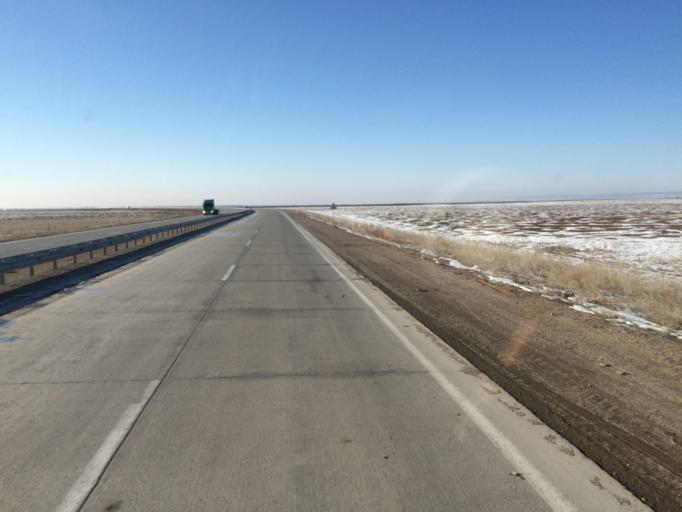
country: KG
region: Chuy
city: Sokuluk
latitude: 43.3461
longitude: 74.3019
